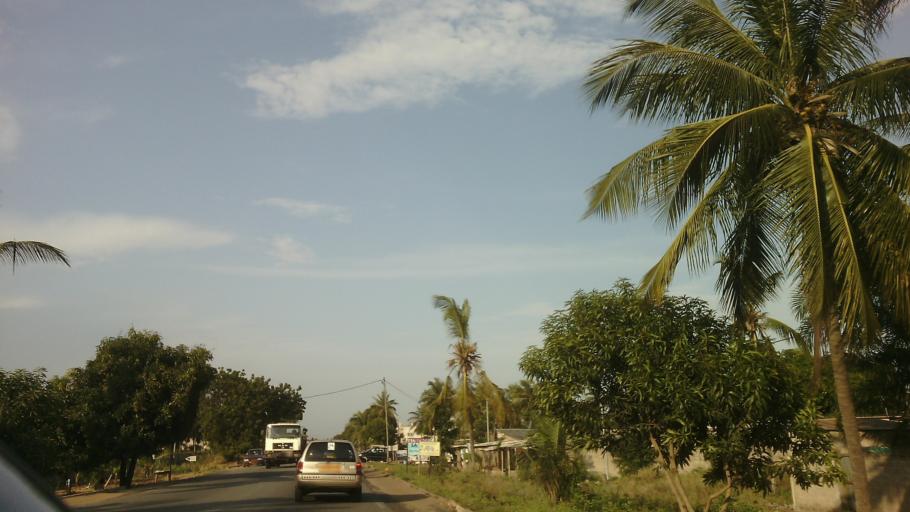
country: TG
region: Maritime
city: Vogan
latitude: 6.1984
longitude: 1.4037
